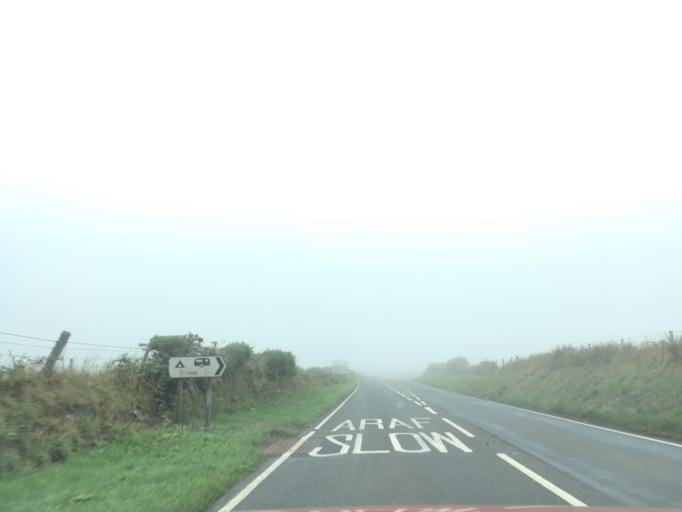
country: GB
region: Wales
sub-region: Pembrokeshire
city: Llanrhian
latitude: 51.8694
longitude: -5.1428
